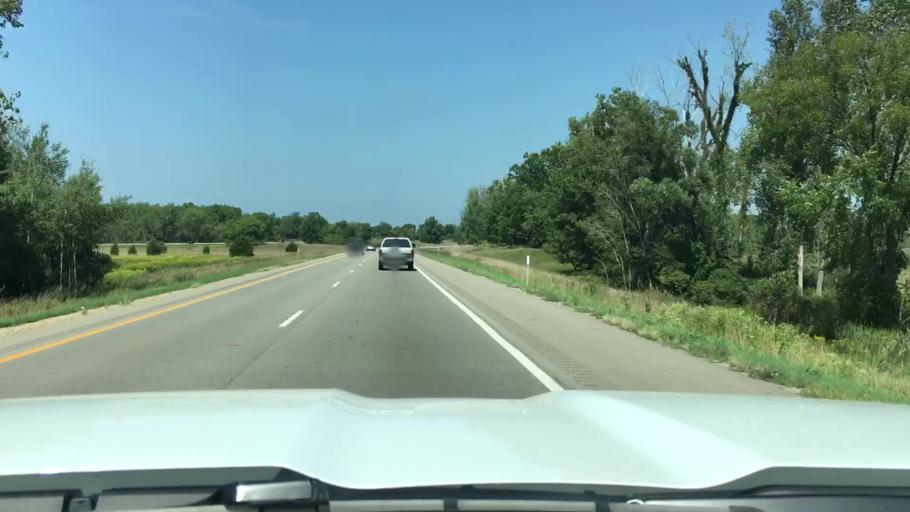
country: US
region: Michigan
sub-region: Kalamazoo County
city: Schoolcraft
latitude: 42.1526
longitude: -85.6415
